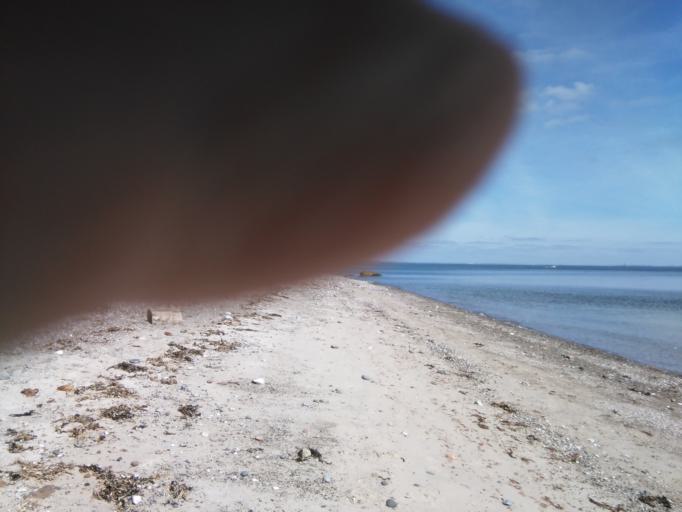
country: DK
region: Central Jutland
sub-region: Arhus Kommune
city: Beder
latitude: 56.0756
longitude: 10.2533
